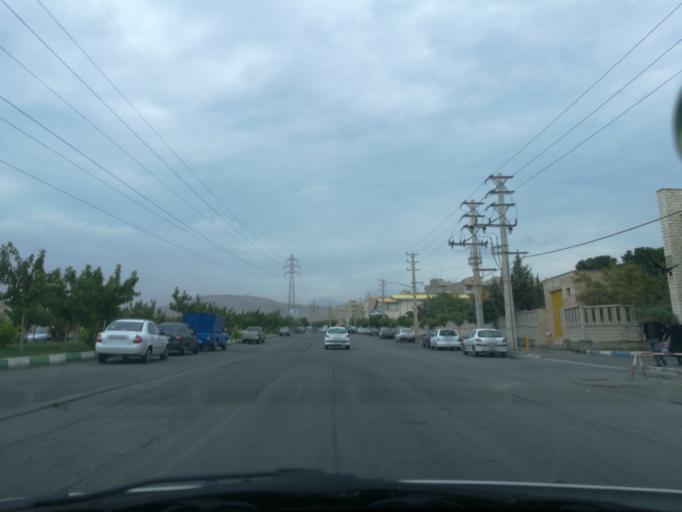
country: IR
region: Alborz
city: Karaj
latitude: 35.8609
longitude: 50.9249
